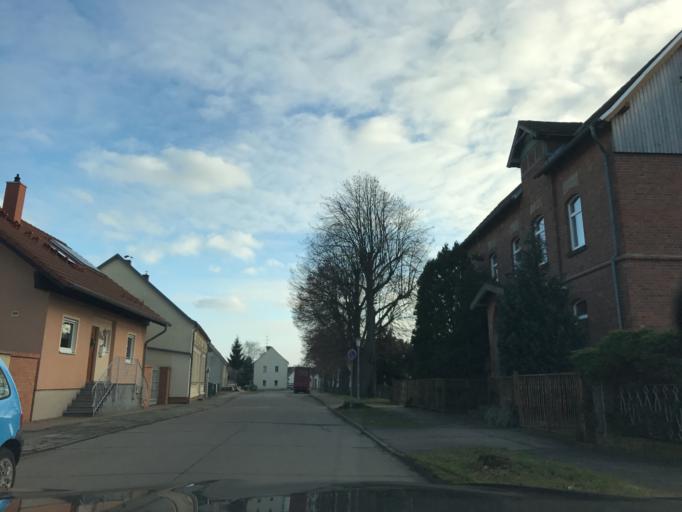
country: DE
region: Brandenburg
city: Ziesar
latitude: 52.2684
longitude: 12.2932
